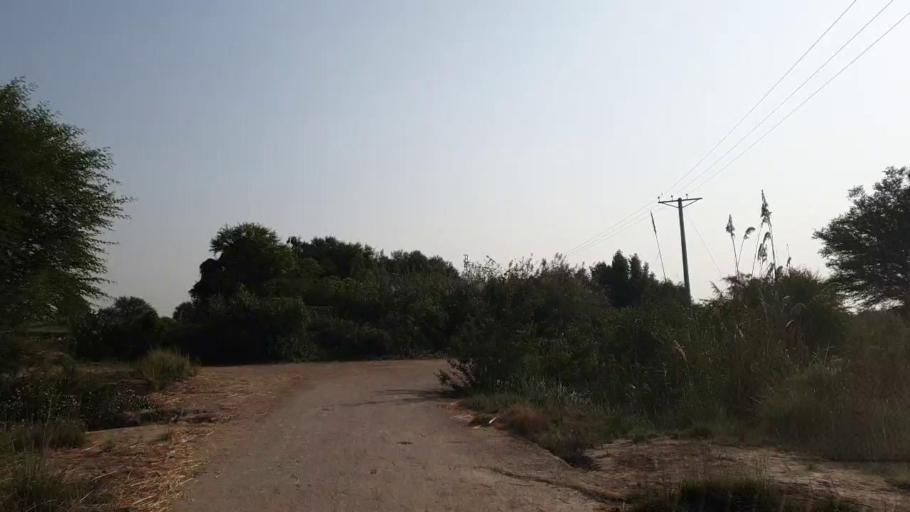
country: PK
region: Sindh
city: Bulri
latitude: 24.9797
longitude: 68.3779
